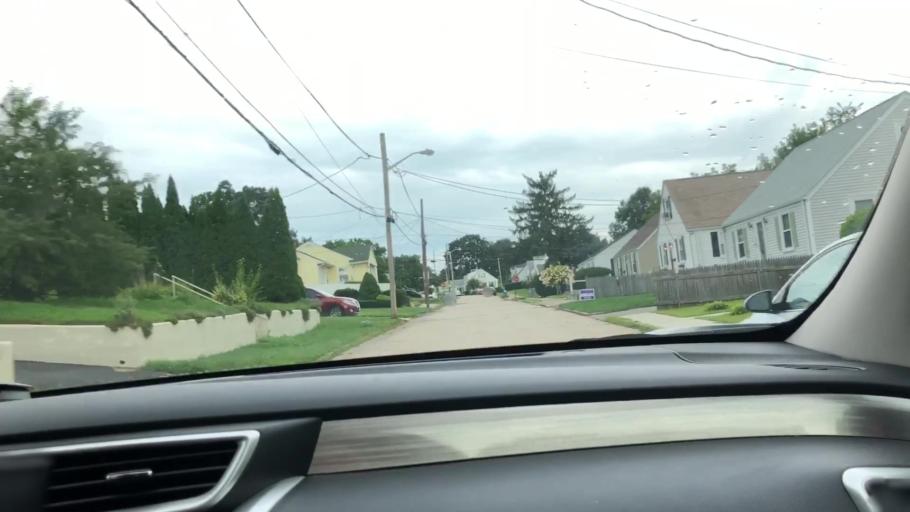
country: US
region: Rhode Island
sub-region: Providence County
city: Central Falls
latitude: 41.8625
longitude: -71.4147
